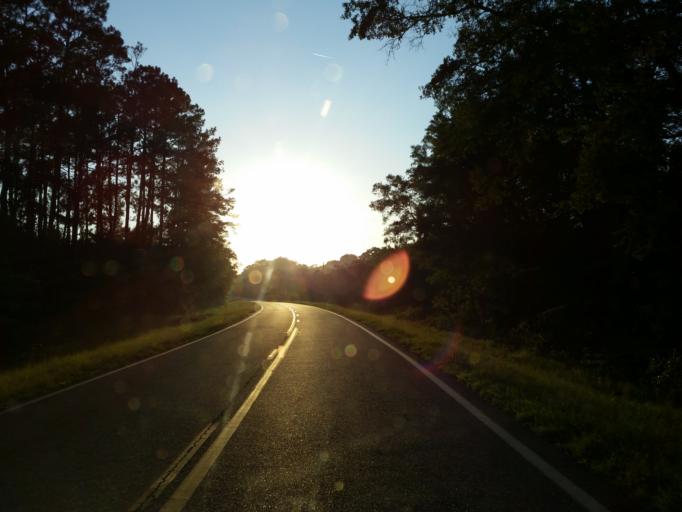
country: US
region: Georgia
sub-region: Berrien County
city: Nashville
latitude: 31.1782
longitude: -83.1278
